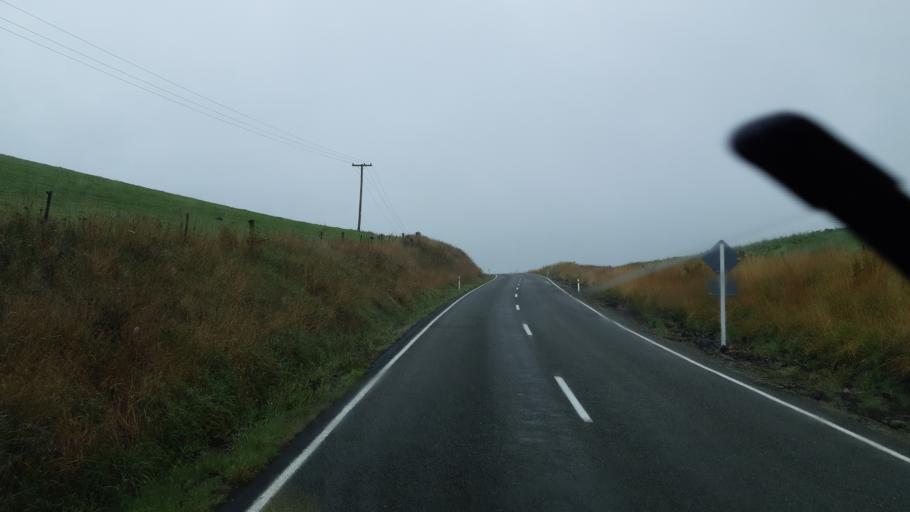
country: NZ
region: Otago
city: Oamaru
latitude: -44.9126
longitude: 170.8355
